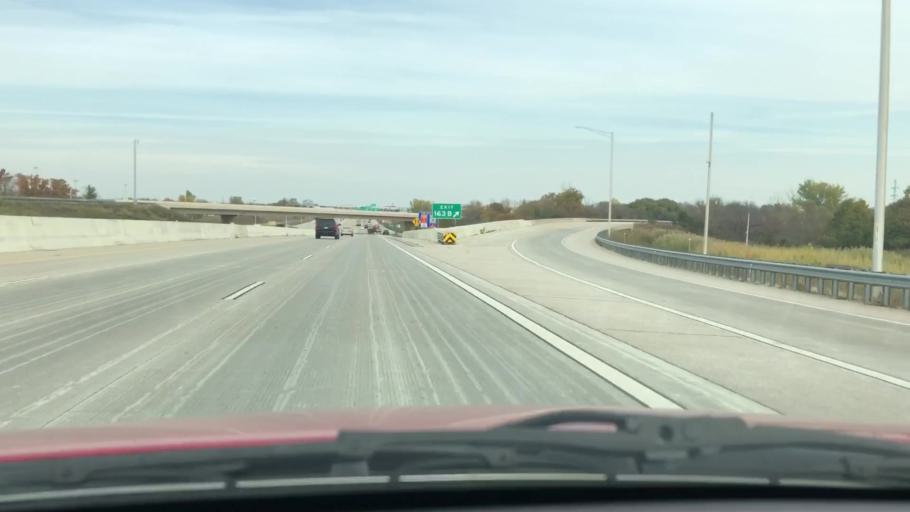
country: US
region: Wisconsin
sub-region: Brown County
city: De Pere
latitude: 44.4538
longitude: -88.0888
